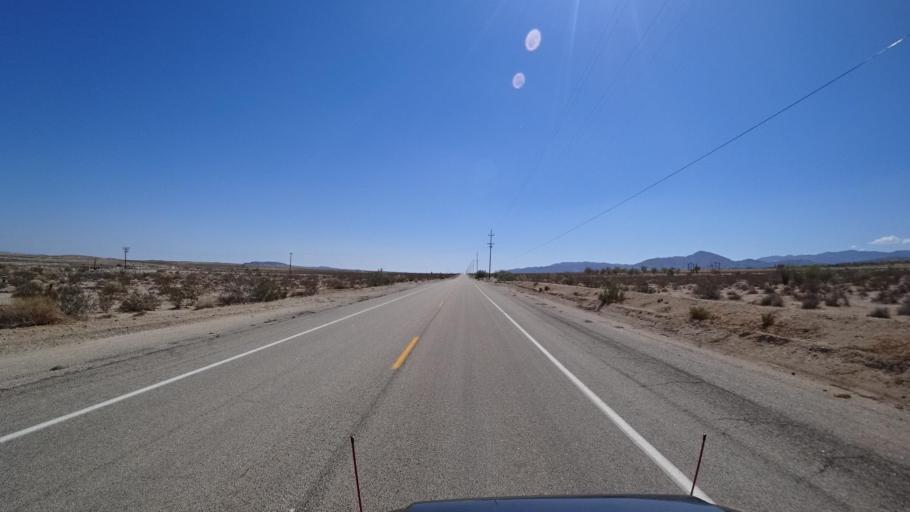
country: US
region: California
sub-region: San Diego County
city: Borrego Springs
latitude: 33.2028
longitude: -116.3164
